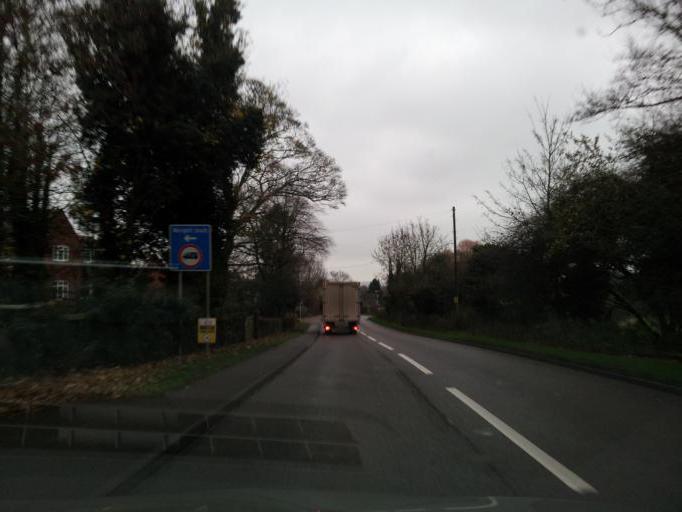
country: GB
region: England
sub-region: Northamptonshire
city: Daventry
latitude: 52.3306
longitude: -1.1762
